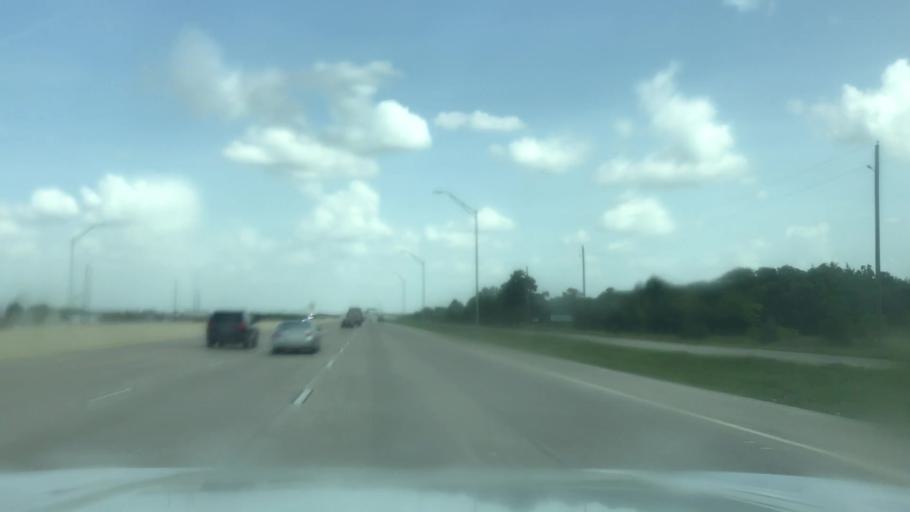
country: US
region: Texas
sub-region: Waller County
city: Waller
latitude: 30.0613
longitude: -95.9032
